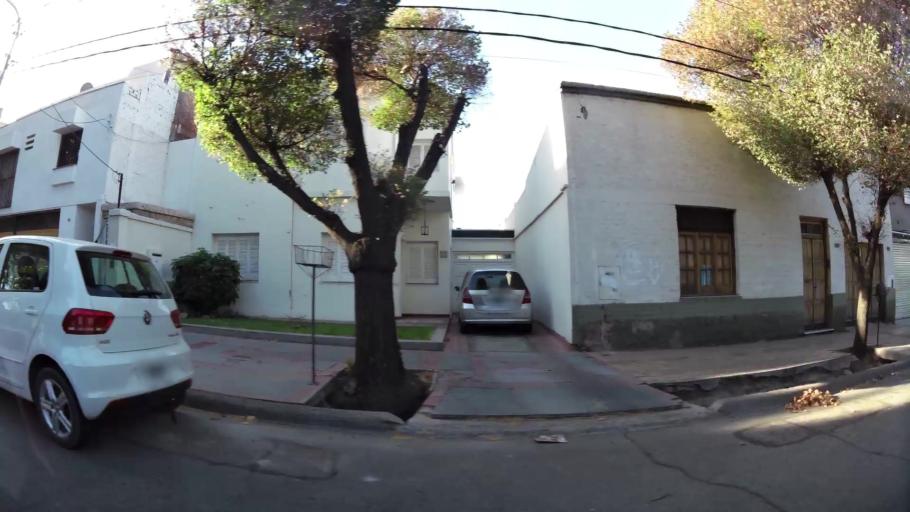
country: AR
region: Mendoza
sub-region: Departamento de Godoy Cruz
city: Godoy Cruz
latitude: -32.9076
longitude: -68.8510
